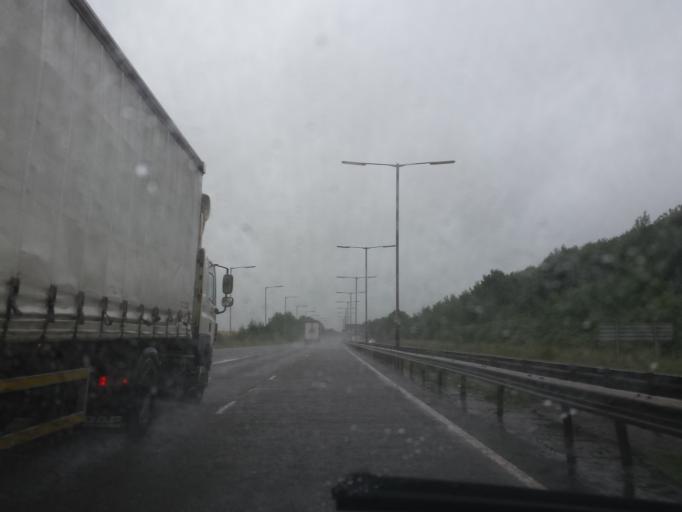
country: GB
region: England
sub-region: Warwickshire
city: Brandon
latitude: 52.4291
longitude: -1.4249
